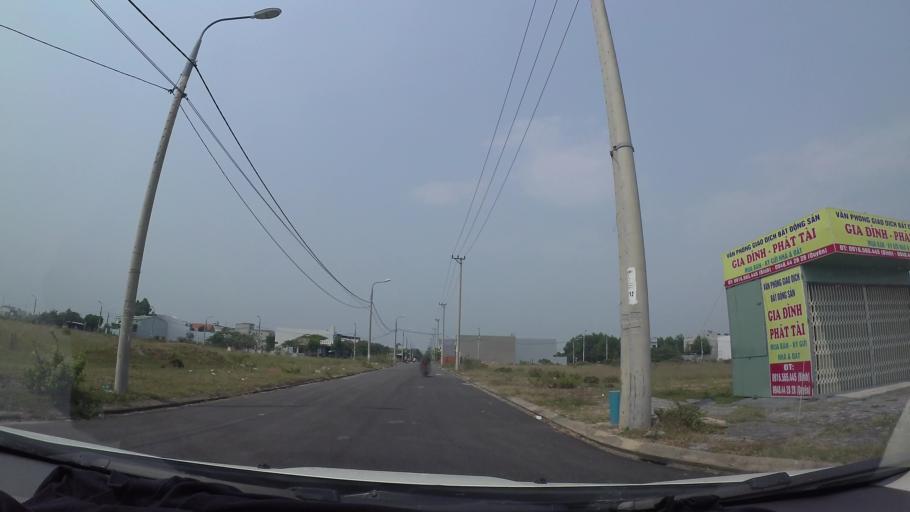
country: VN
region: Da Nang
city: Cam Le
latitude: 15.9798
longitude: 108.2169
